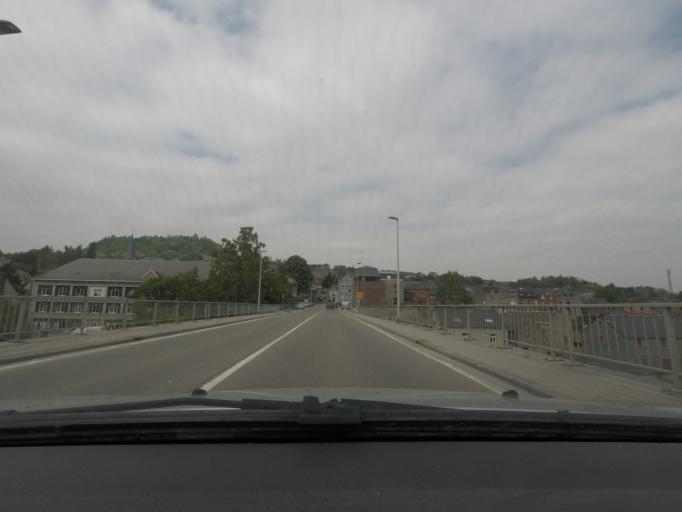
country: BE
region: Wallonia
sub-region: Province de Namur
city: Noville-les-Bois
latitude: 50.4684
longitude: 4.9947
